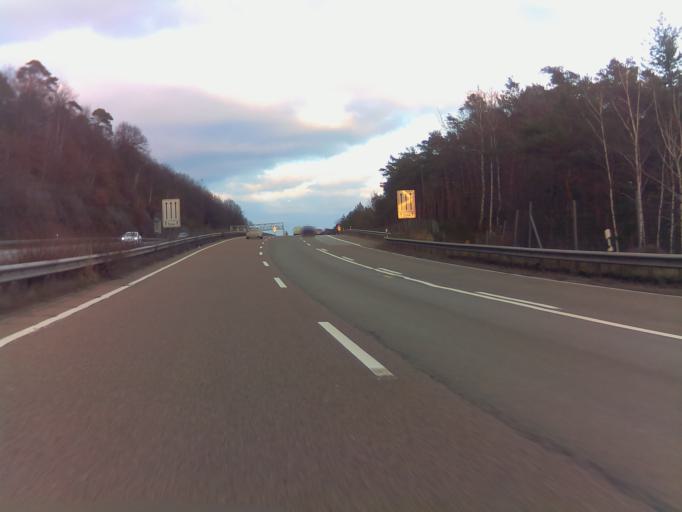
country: DE
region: Rheinland-Pfalz
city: Carlsberg
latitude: 49.5172
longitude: 8.0321
